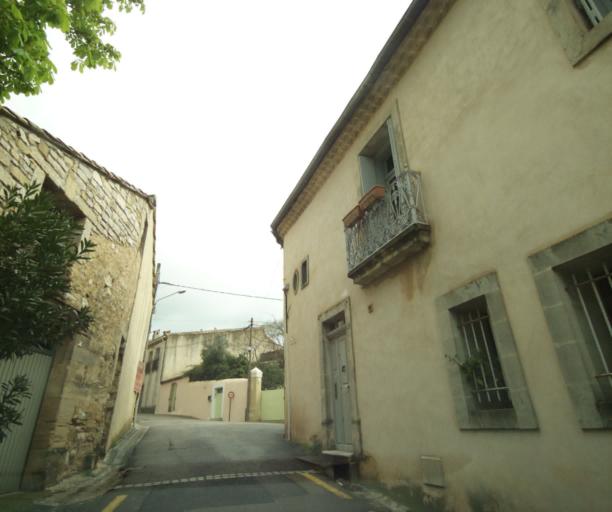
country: FR
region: Languedoc-Roussillon
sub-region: Departement de l'Herault
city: Murviel-les-Montpellier
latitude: 43.6043
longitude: 3.7355
